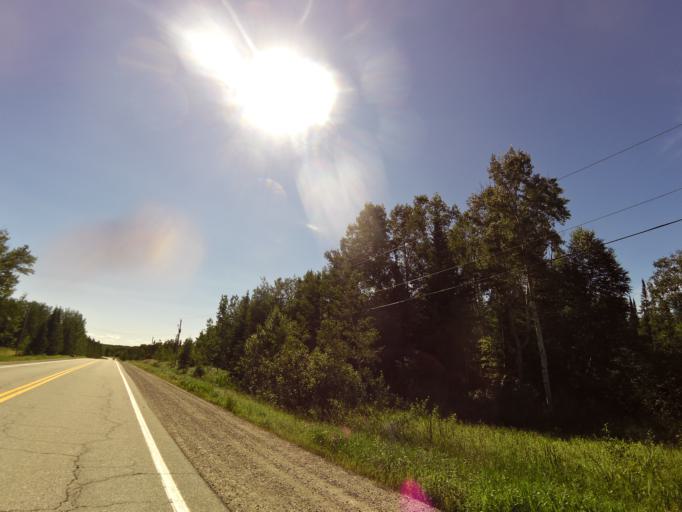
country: CA
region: Quebec
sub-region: Abitibi-Temiscamingue
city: Senneterre
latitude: 48.2285
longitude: -77.3376
